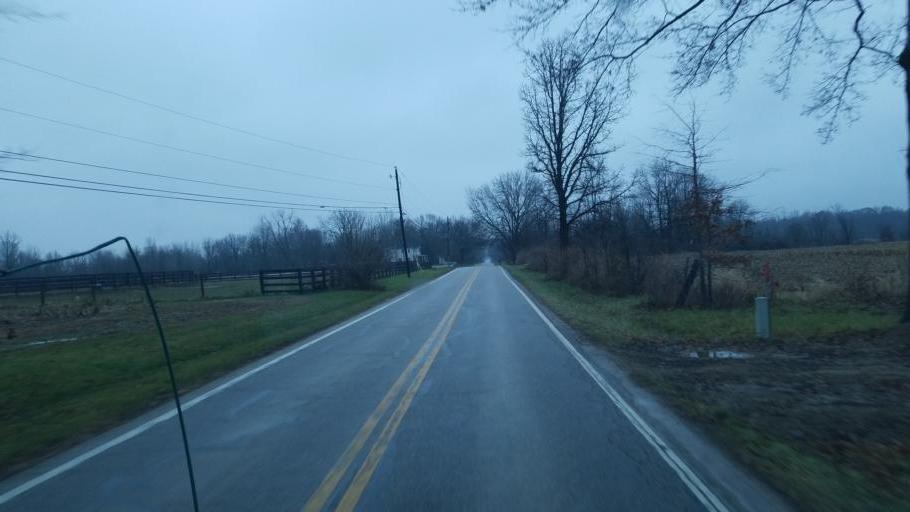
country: US
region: Ohio
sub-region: Delaware County
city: Delaware
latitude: 40.2794
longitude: -83.0466
